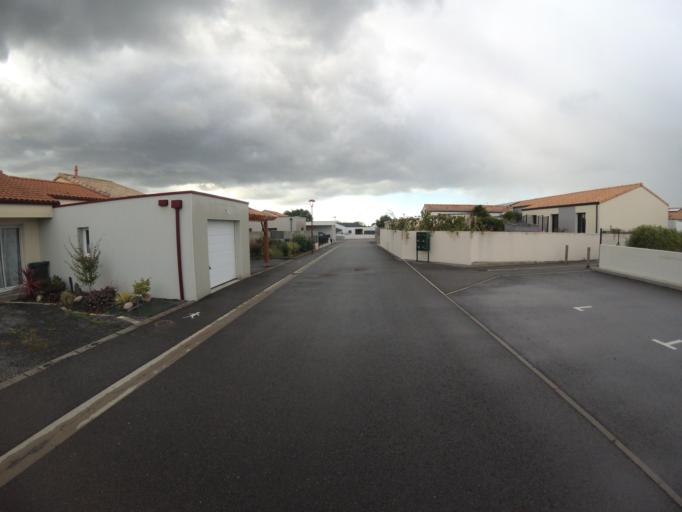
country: FR
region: Pays de la Loire
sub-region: Departement de la Loire-Atlantique
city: Saint-Hilaire-de-Clisson
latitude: 47.0664
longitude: -1.3111
